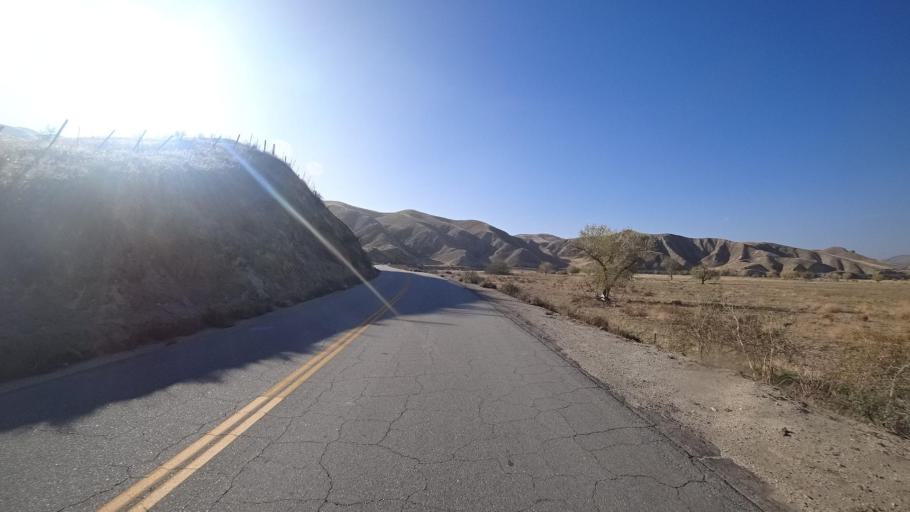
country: US
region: California
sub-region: Kern County
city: Arvin
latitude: 35.3094
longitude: -118.6992
